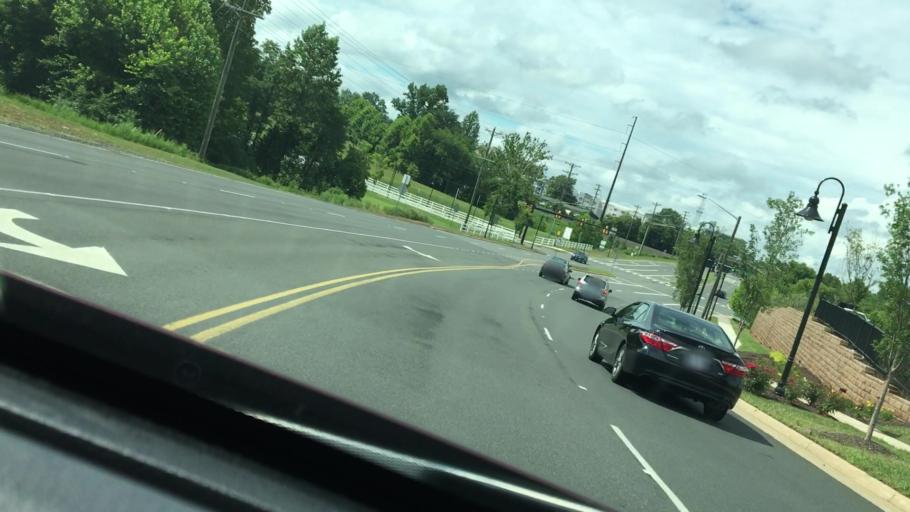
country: US
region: Virginia
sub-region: Prince William County
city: Buckhall
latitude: 38.7614
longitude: -77.4420
